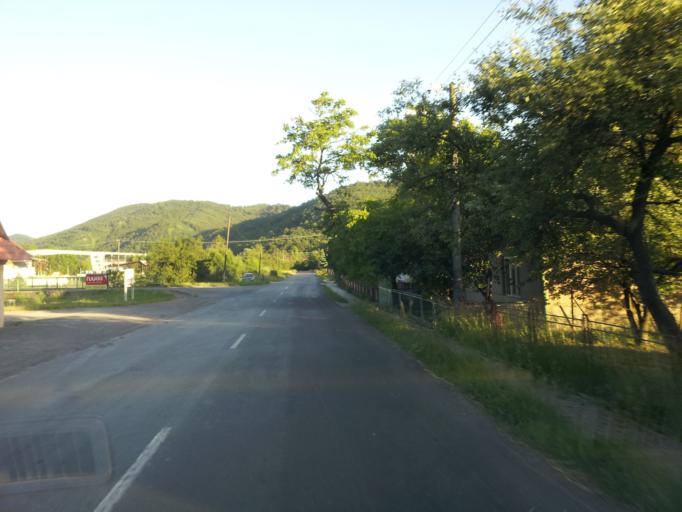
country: SK
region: Banskobystricky
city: Svaety Anton
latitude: 48.3535
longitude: 18.9270
